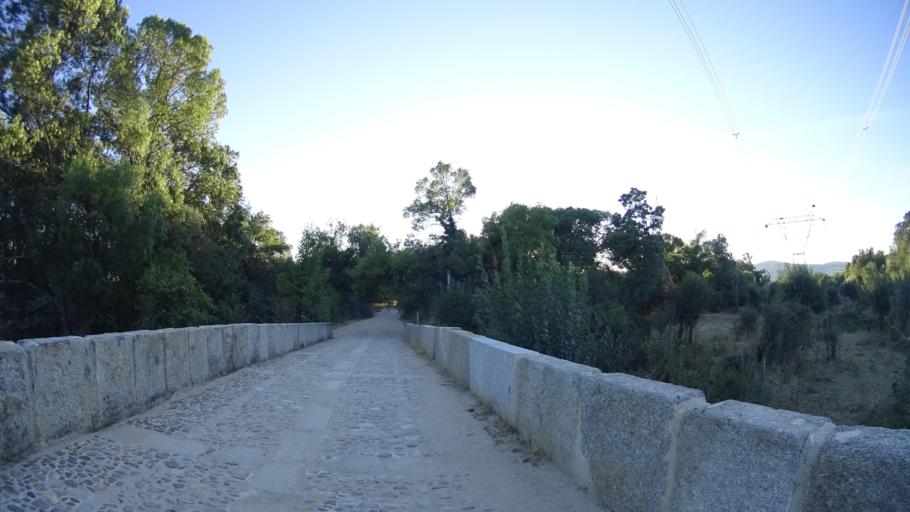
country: ES
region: Madrid
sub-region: Provincia de Madrid
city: Navalquejigo
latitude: 40.6375
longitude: -4.0564
